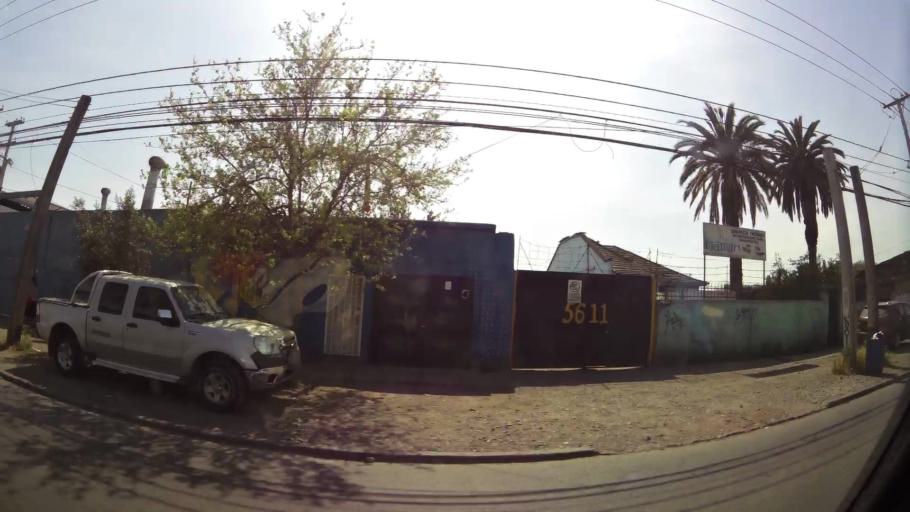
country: CL
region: Santiago Metropolitan
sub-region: Provincia de Santiago
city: Lo Prado
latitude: -33.4268
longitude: -70.7128
